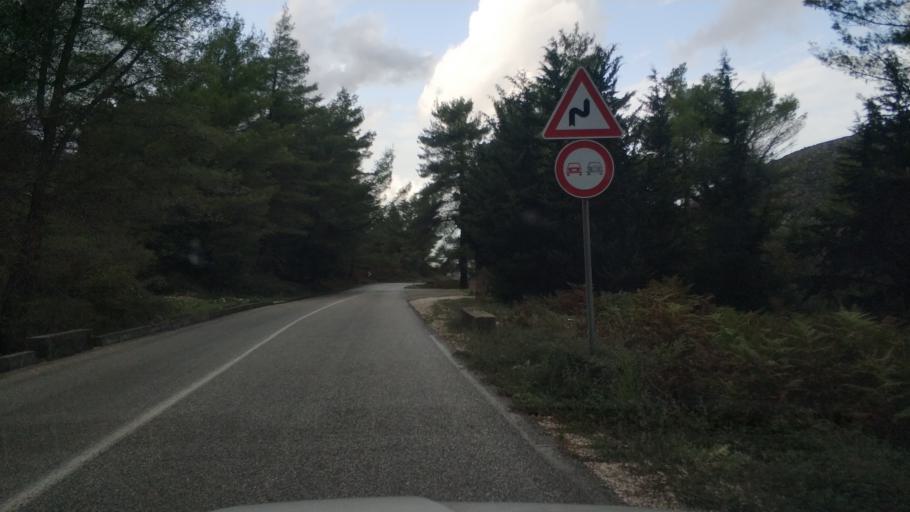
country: AL
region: Vlore
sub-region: Rrethi i Vlores
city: Orikum
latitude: 40.2524
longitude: 19.5378
